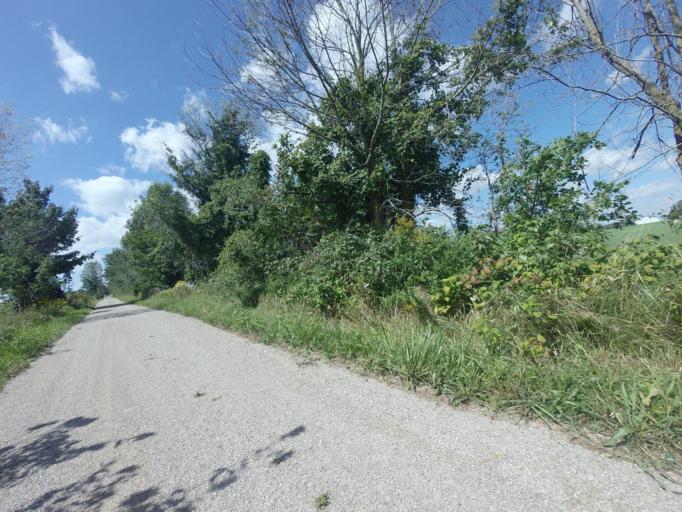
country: CA
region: Ontario
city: Huron East
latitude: 43.6705
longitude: -81.2759
